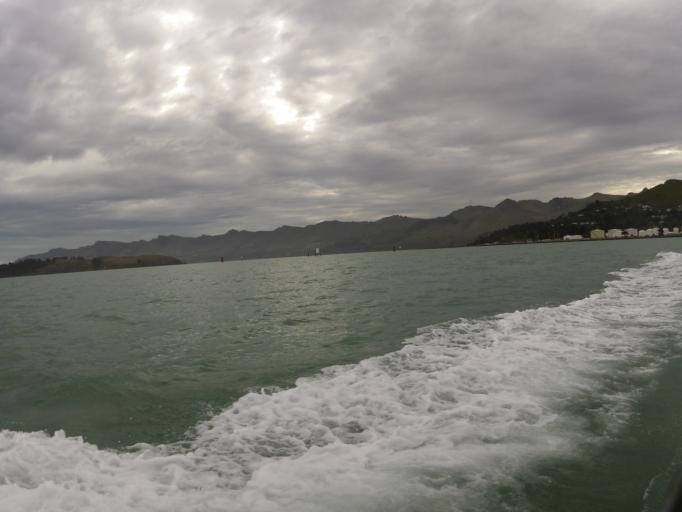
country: NZ
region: Canterbury
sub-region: Christchurch City
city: Christchurch
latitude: -43.6104
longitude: 172.7185
